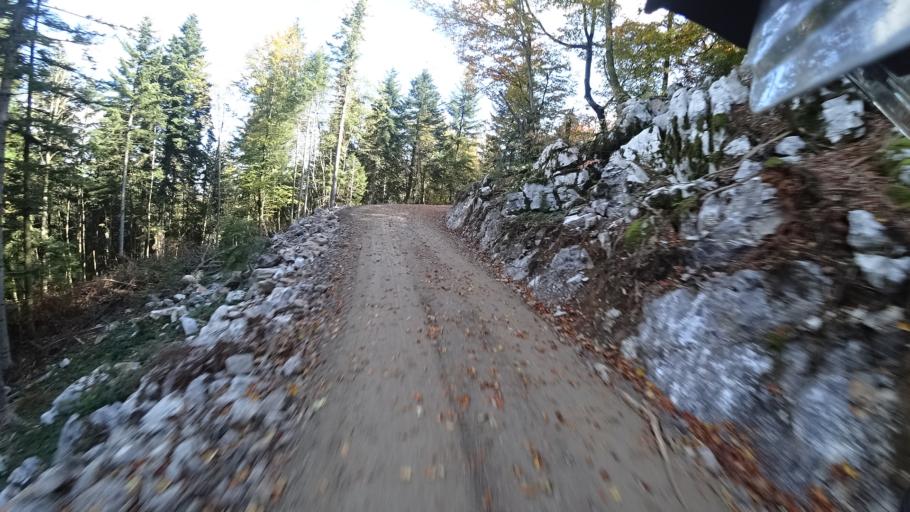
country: HR
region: Karlovacka
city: Plaski
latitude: 45.0638
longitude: 15.3449
